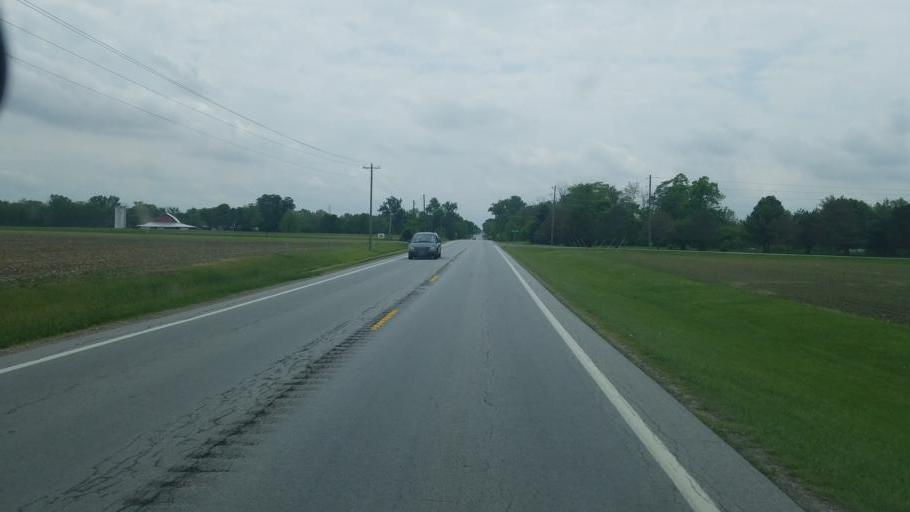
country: US
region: Ohio
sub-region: Union County
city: Richwood
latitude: 40.3517
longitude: -83.3014
